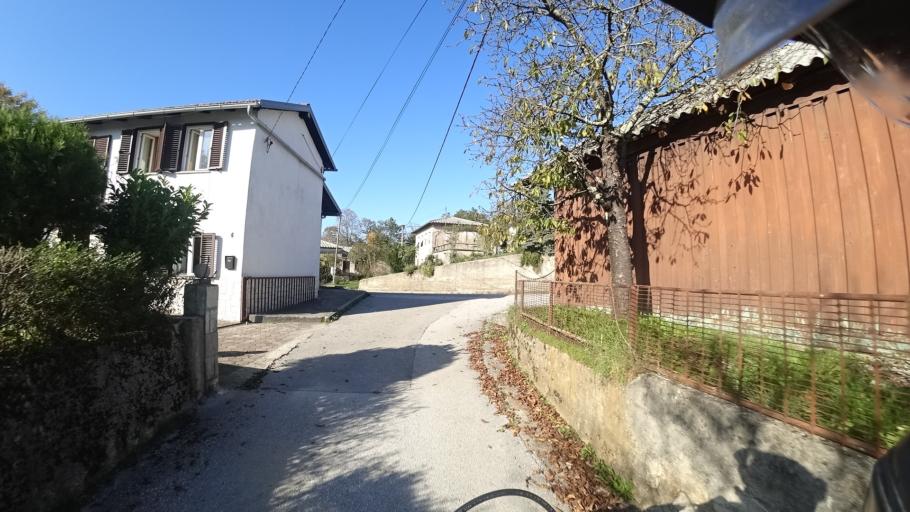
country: HR
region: Primorsko-Goranska
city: Klana
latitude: 45.4221
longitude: 14.3442
